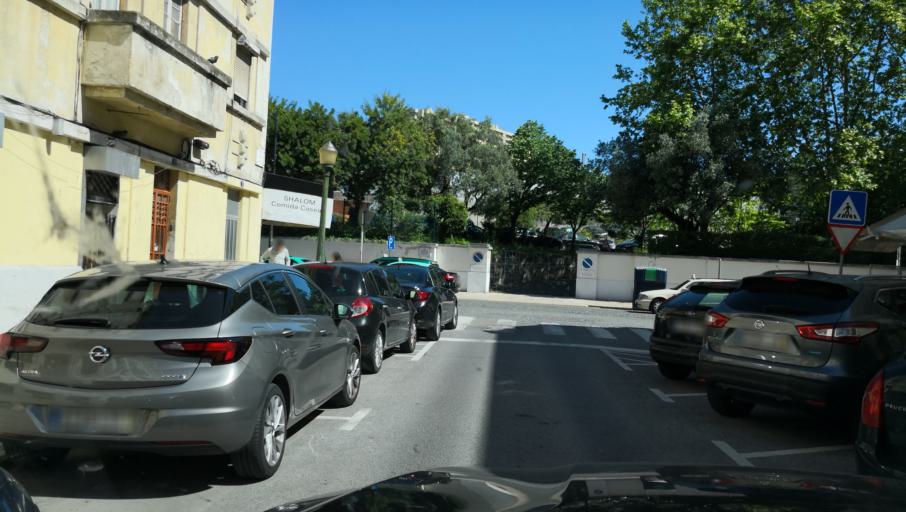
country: PT
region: Lisbon
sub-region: Lisbon
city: Lisbon
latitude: 38.7398
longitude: -9.1649
